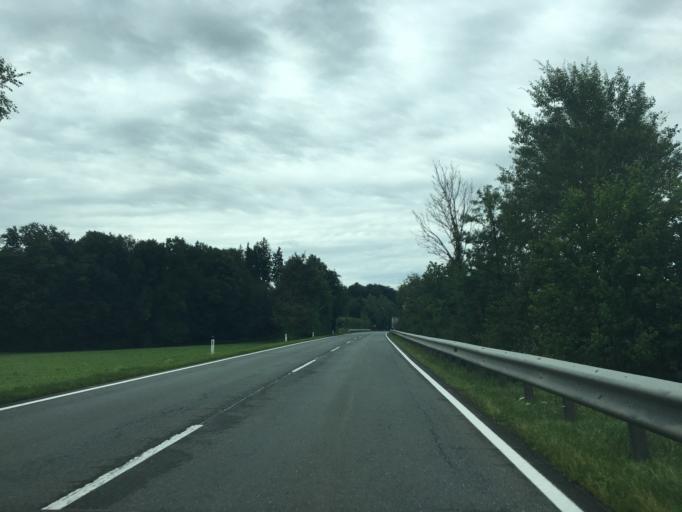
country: AT
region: Salzburg
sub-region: Politischer Bezirk Salzburg-Umgebung
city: Lamprechtshausen
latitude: 48.0155
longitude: 12.9660
